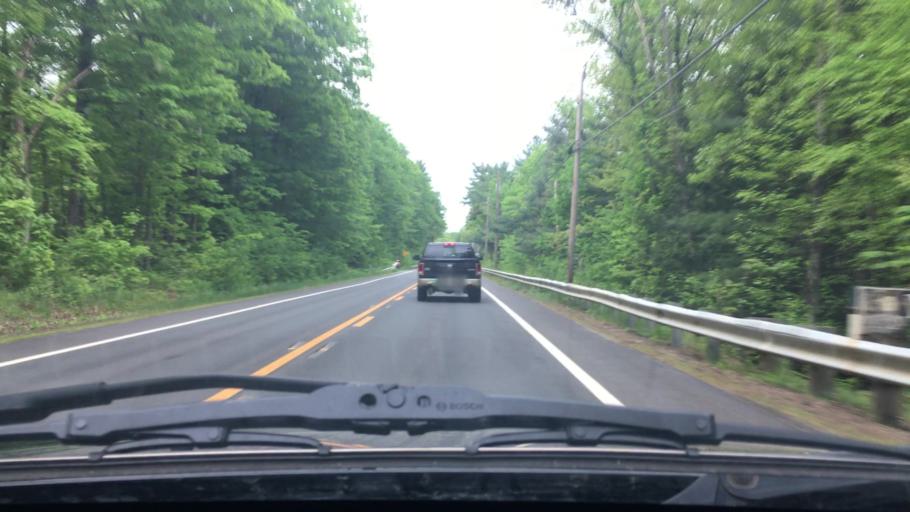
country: US
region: Massachusetts
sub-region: Franklin County
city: Leverett
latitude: 42.4729
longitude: -72.5136
